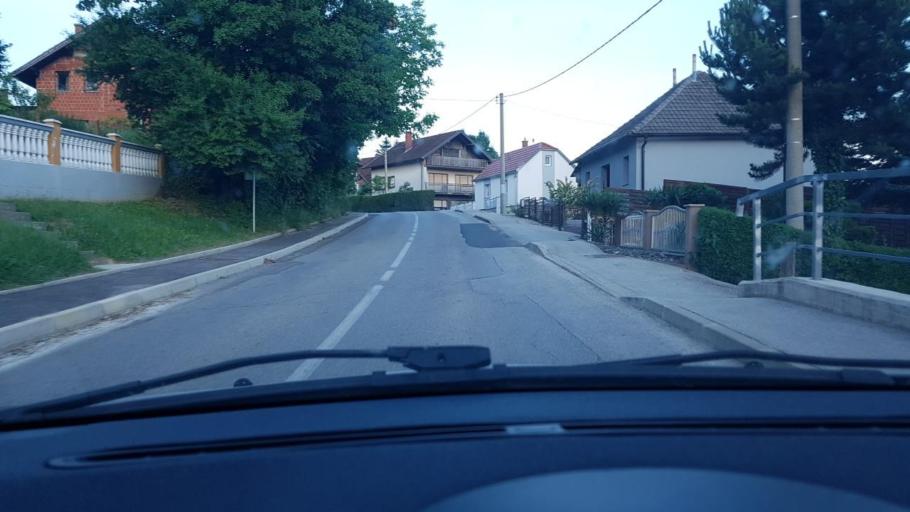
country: HR
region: Varazdinska
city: Remetinec
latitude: 46.1813
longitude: 16.3313
